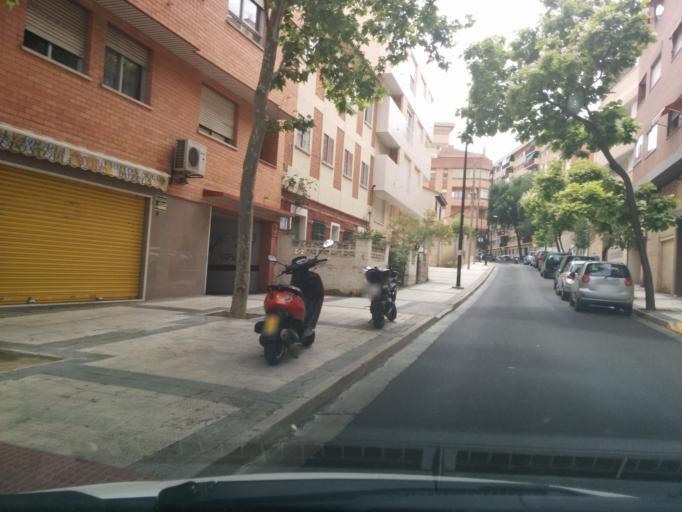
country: ES
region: Aragon
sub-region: Provincia de Zaragoza
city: Zaragoza
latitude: 41.6270
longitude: -0.8756
